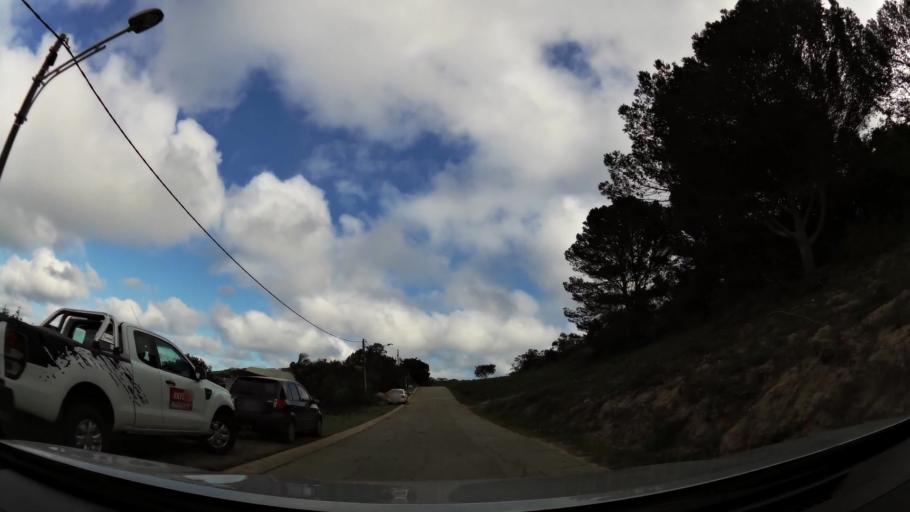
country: ZA
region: Western Cape
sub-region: Eden District Municipality
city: Plettenberg Bay
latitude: -34.0812
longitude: 23.3614
